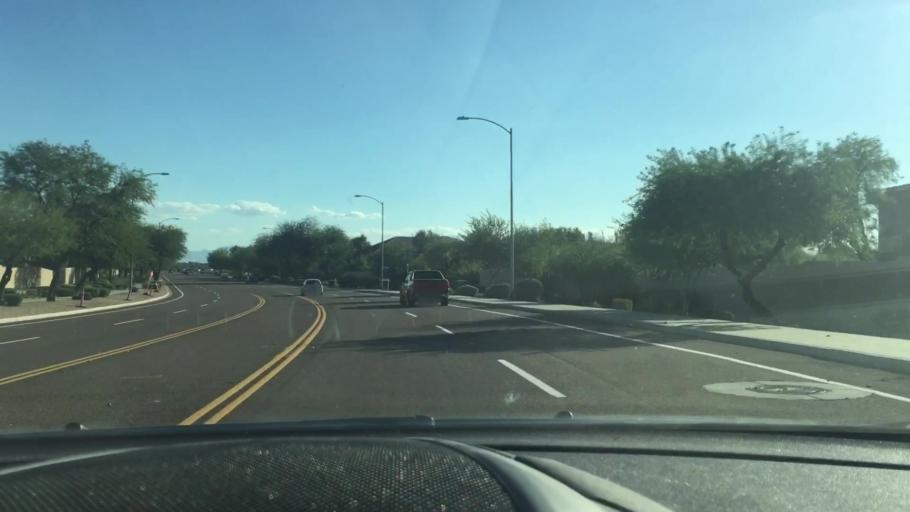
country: US
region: Arizona
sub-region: Maricopa County
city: Sun City West
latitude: 33.7071
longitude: -112.2375
